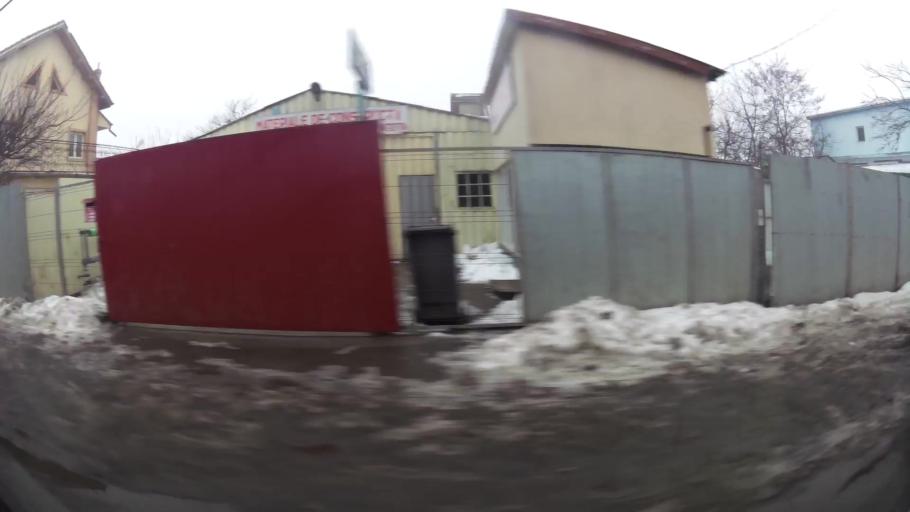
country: RO
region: Ilfov
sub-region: Comuna Chiajna
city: Chiajna
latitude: 44.4614
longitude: 25.9838
